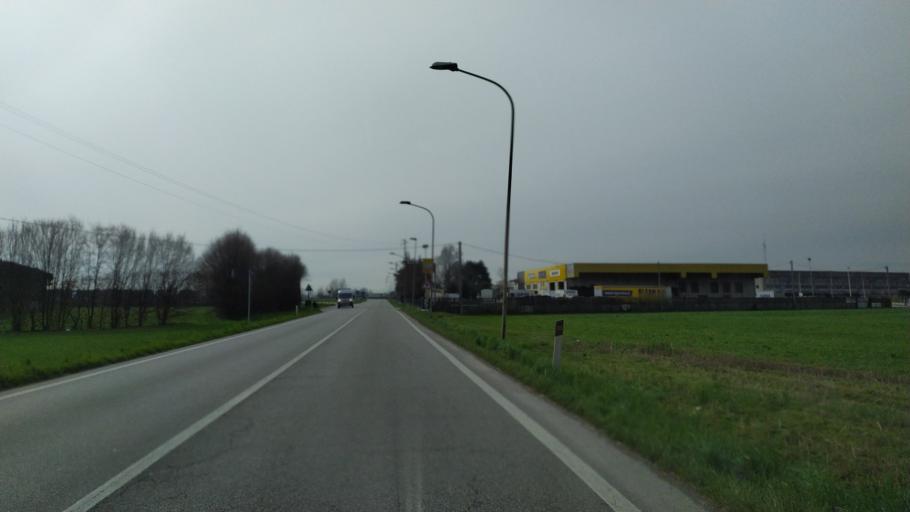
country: IT
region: Veneto
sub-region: Provincia di Padova
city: Carmignano di Brenta
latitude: 45.6192
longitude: 11.6975
